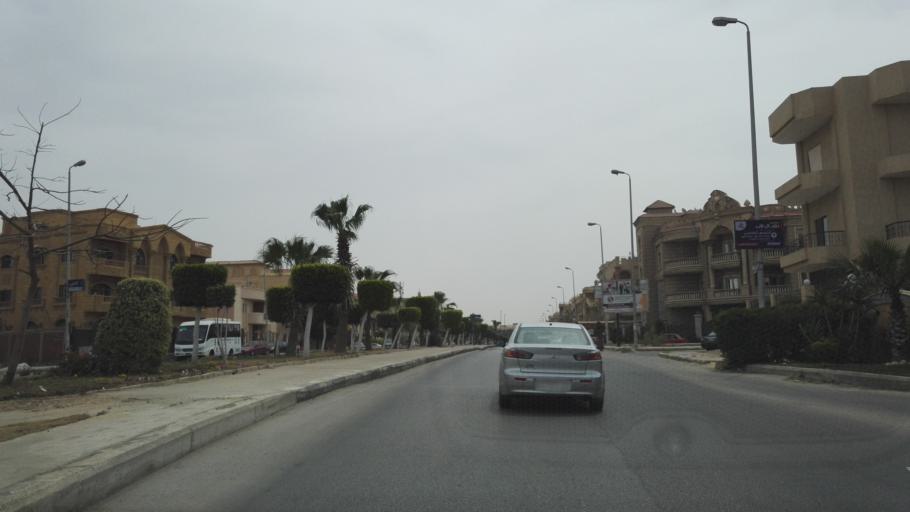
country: EG
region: Muhafazat al Qahirah
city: Cairo
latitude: 30.0046
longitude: 31.4178
